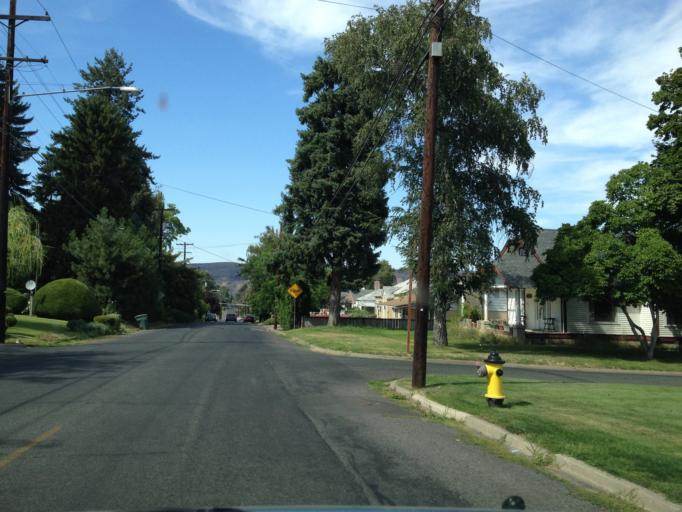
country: US
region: Washington
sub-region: Yakima County
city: Yakima
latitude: 46.5979
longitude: -120.5513
